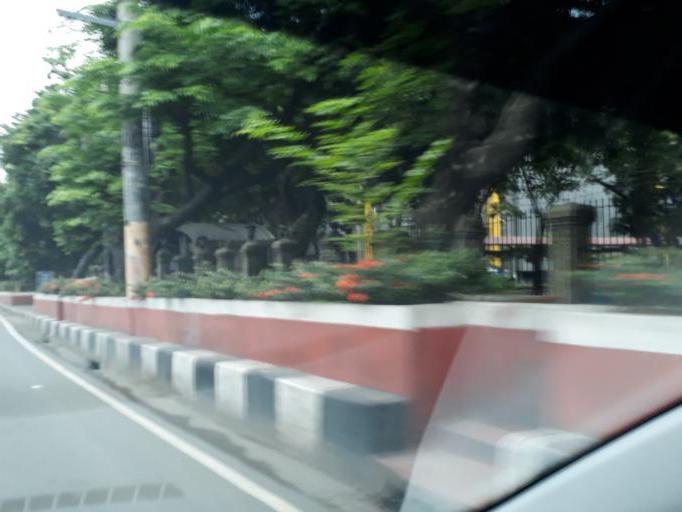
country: PH
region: Metro Manila
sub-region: City of Manila
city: Manila
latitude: 14.6095
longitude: 120.9924
